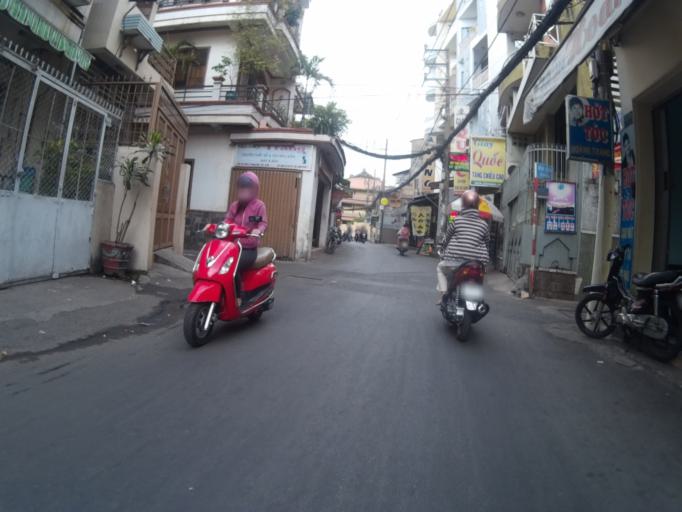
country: VN
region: Ho Chi Minh City
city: Quan Tan Phu
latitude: 10.7799
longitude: 106.6522
